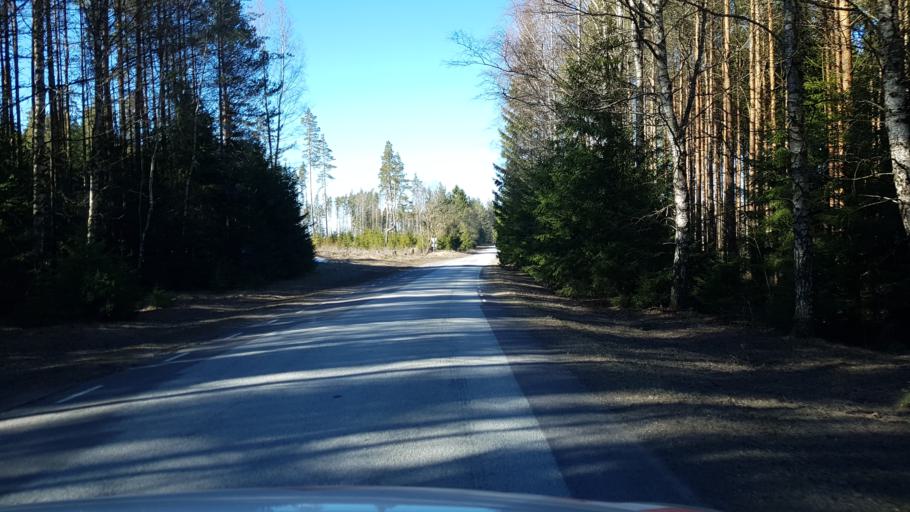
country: EE
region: Laeaene-Virumaa
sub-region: Viru-Nigula vald
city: Kunda
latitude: 59.3740
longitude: 26.5789
